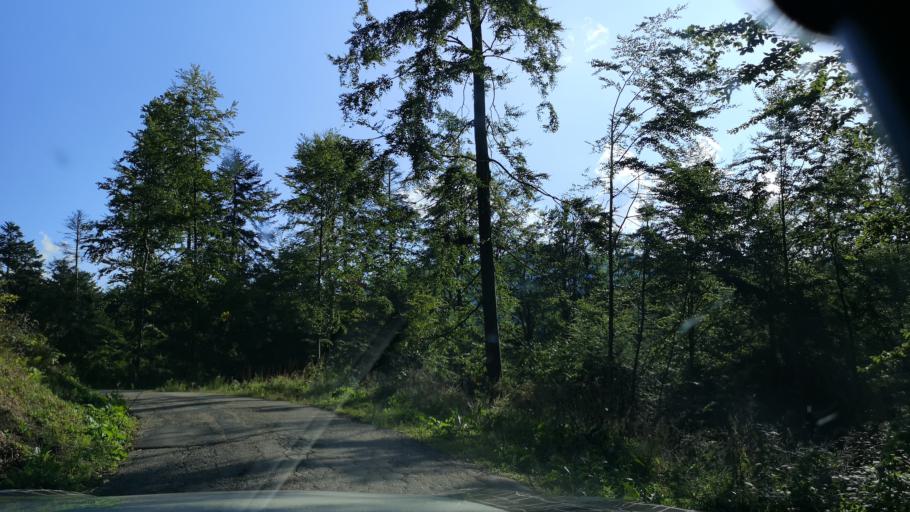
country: DE
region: Baden-Wuerttemberg
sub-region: Karlsruhe Region
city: Bad Herrenalb
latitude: 48.7732
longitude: 8.4349
